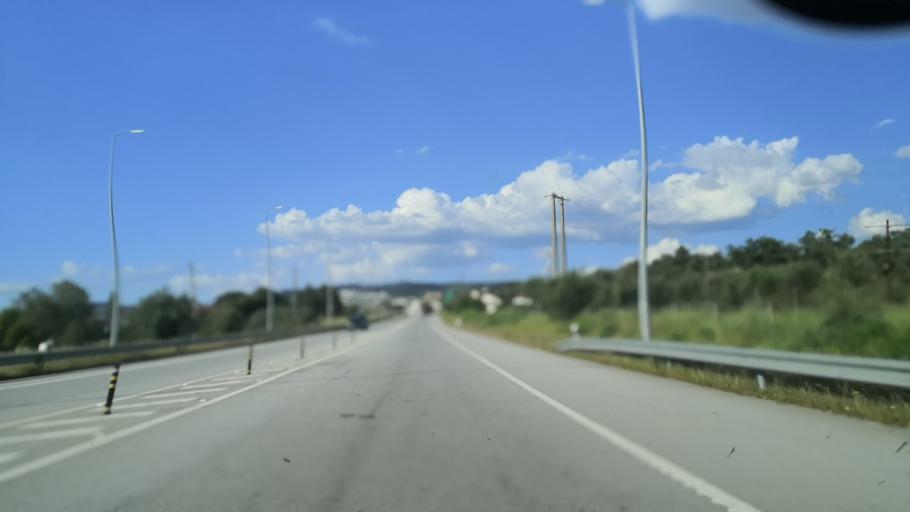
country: PT
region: Portalegre
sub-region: Portalegre
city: Portalegre
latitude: 39.2710
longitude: -7.4386
